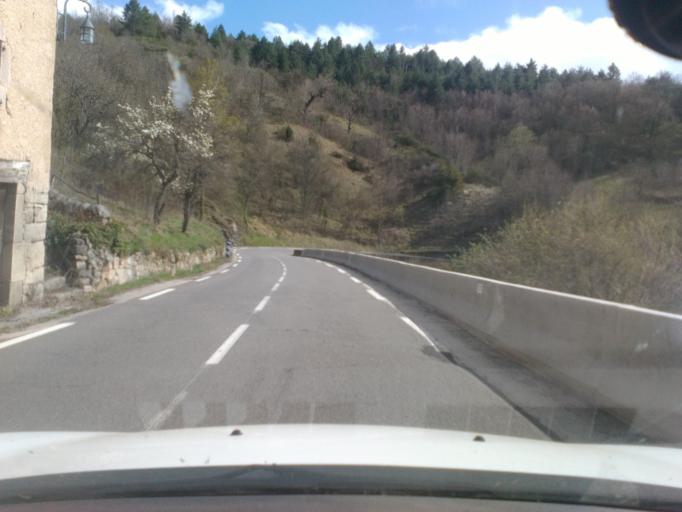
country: FR
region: Languedoc-Roussillon
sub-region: Departement de la Lozere
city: Florac
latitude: 44.4000
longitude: 3.5706
